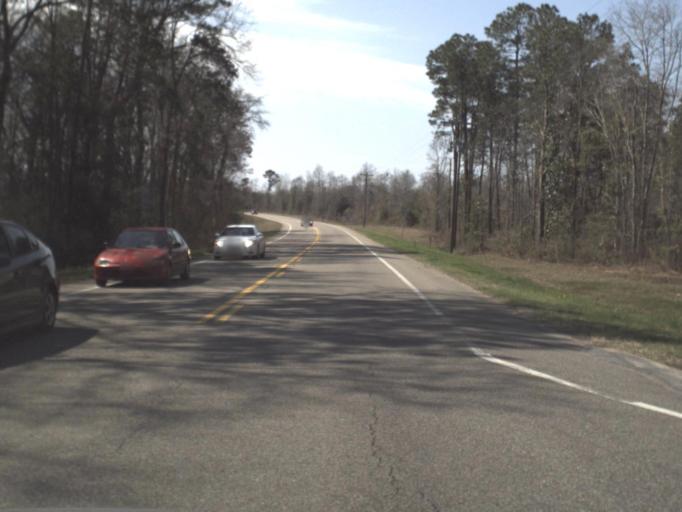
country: US
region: Florida
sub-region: Gadsden County
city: Gretna
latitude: 30.5889
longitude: -84.6901
